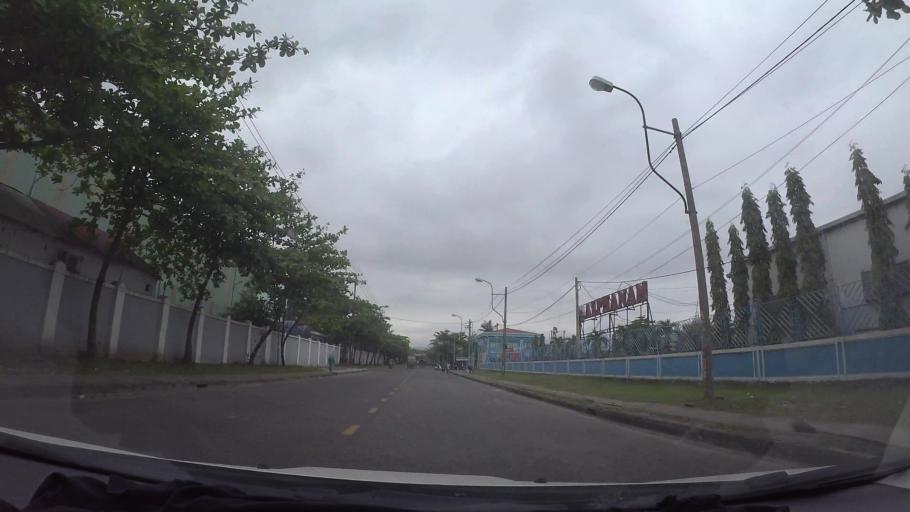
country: VN
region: Da Nang
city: Lien Chieu
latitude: 16.0821
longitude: 108.1412
